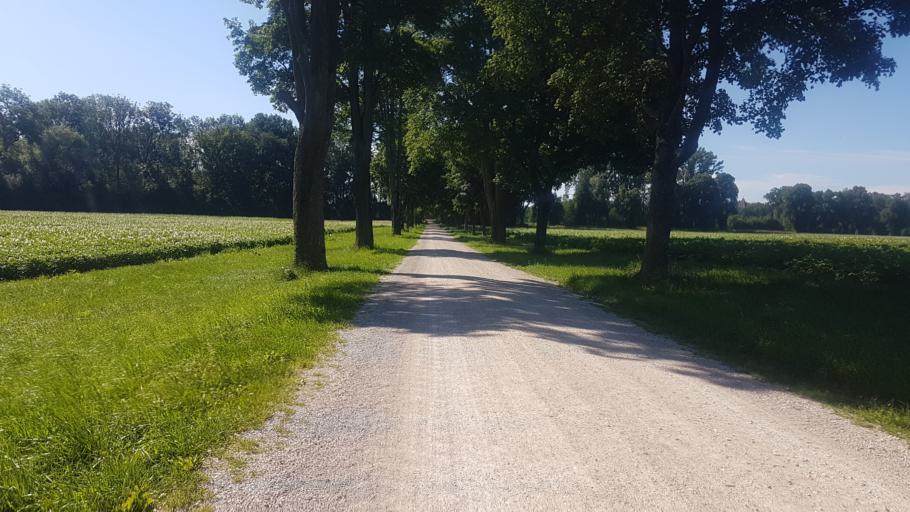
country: DE
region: Bavaria
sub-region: Upper Bavaria
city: Bergheim
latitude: 48.7352
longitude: 11.2665
